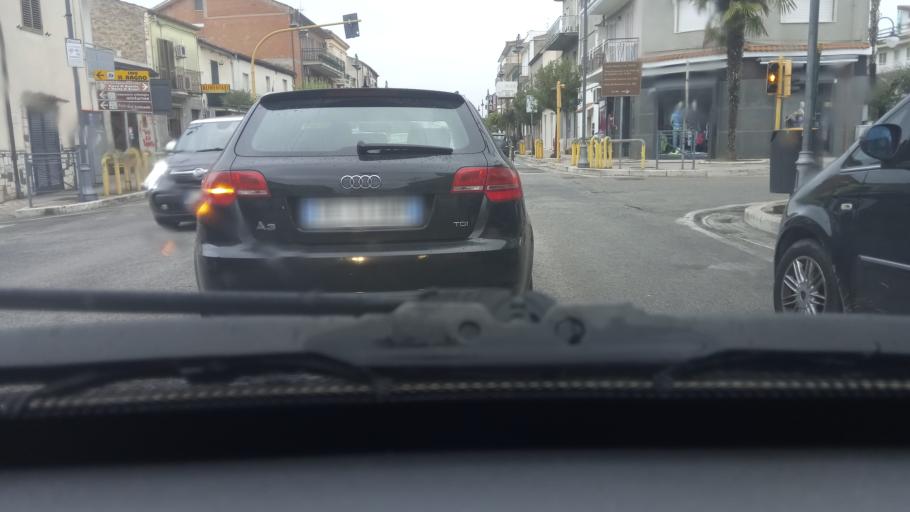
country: IT
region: Latium
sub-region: Provincia di Latina
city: Minturno
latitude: 41.2488
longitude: 13.7409
